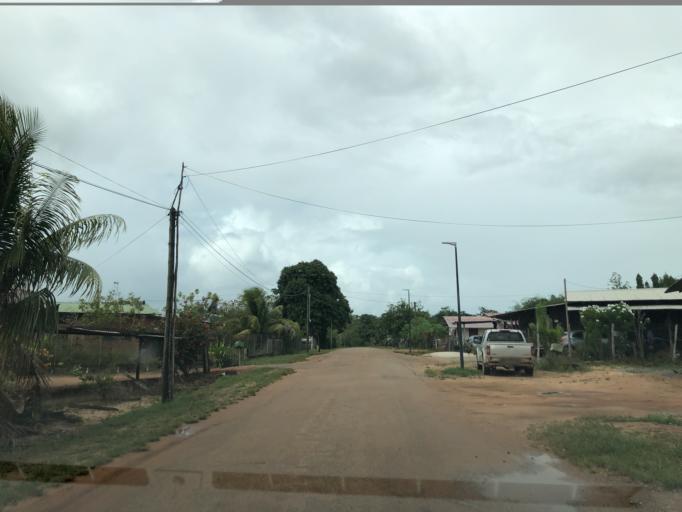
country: GF
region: Guyane
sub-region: Guyane
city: Mana
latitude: 5.6058
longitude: -53.8175
